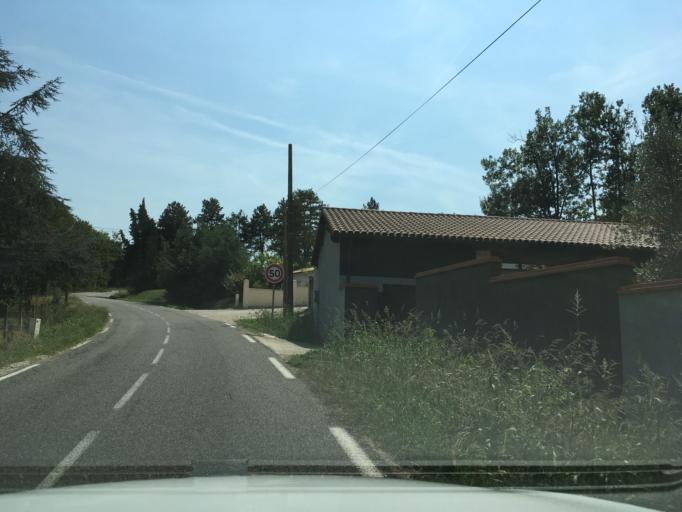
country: FR
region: Midi-Pyrenees
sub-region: Departement du Tarn-et-Garonne
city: Bressols
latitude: 43.9781
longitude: 1.3667
